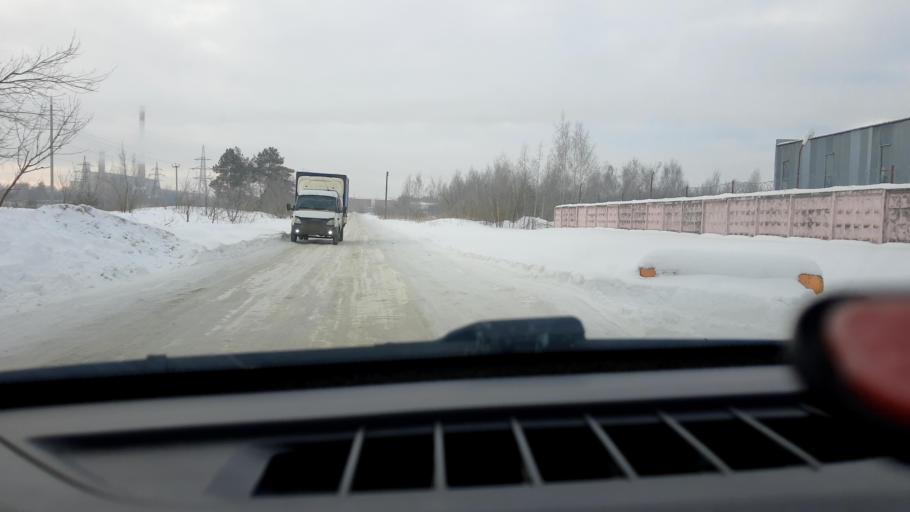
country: RU
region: Nizjnij Novgorod
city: Babino
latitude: 56.2601
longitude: 43.6123
